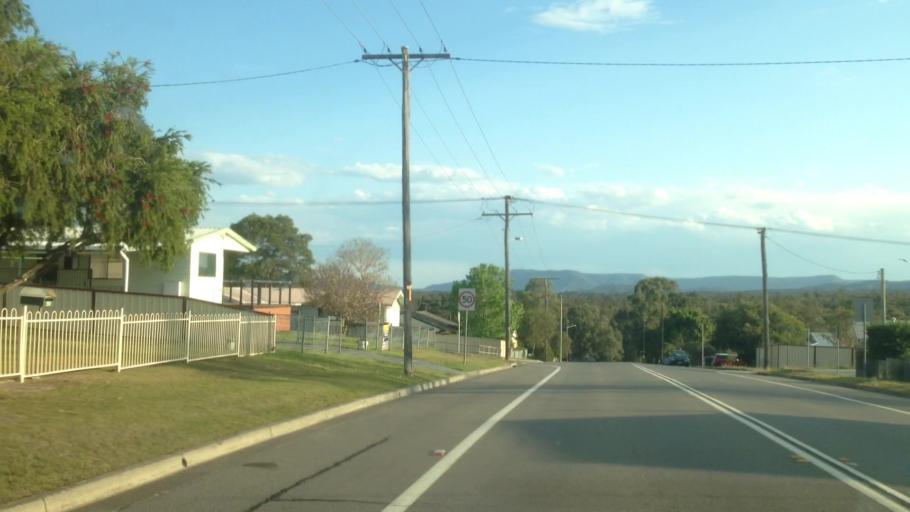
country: AU
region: New South Wales
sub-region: Cessnock
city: Kurri Kurri
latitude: -32.8315
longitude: 151.4809
